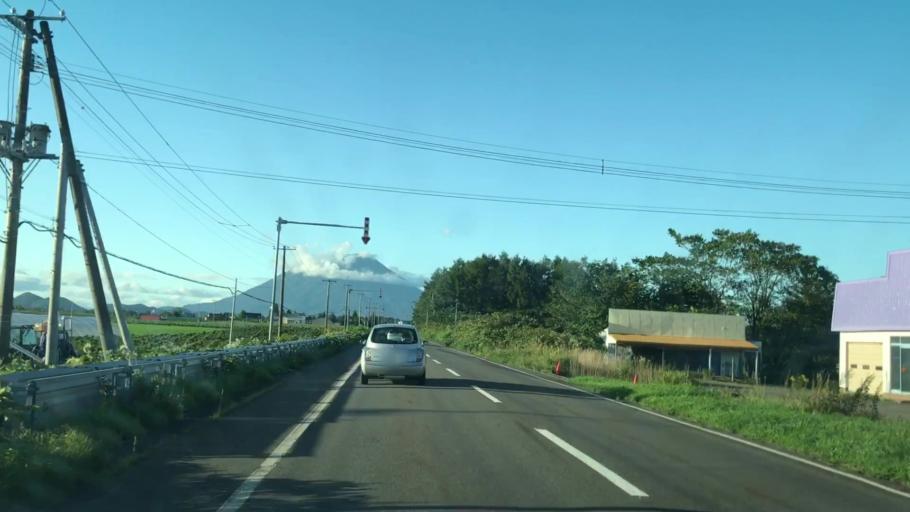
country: JP
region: Hokkaido
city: Niseko Town
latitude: 42.6537
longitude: 140.8111
